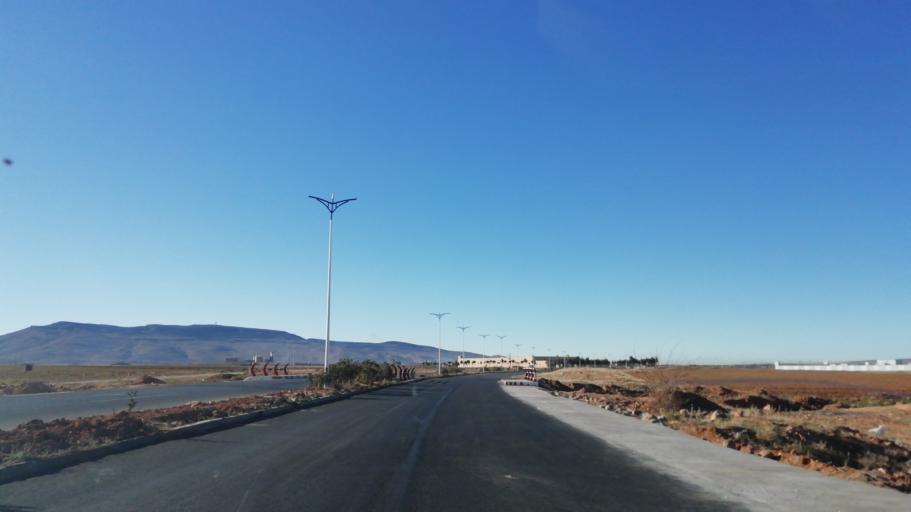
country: DZ
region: El Bayadh
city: El Bayadh
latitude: 33.6947
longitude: 1.0802
